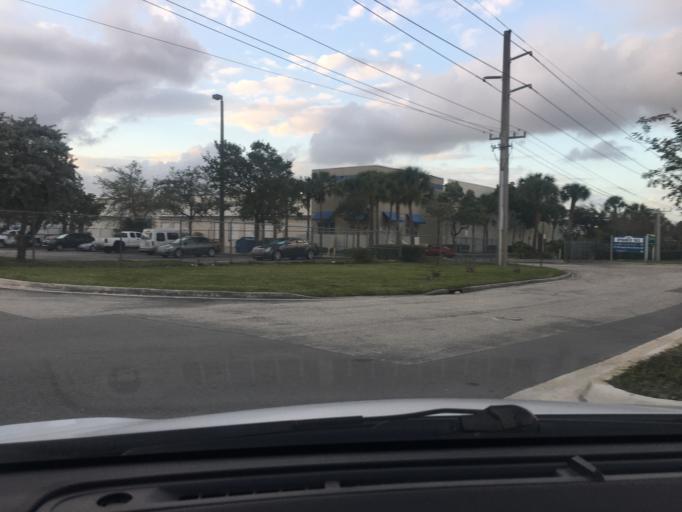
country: US
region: Florida
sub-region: Broward County
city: Dania Beach
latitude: 26.0740
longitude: -80.1746
